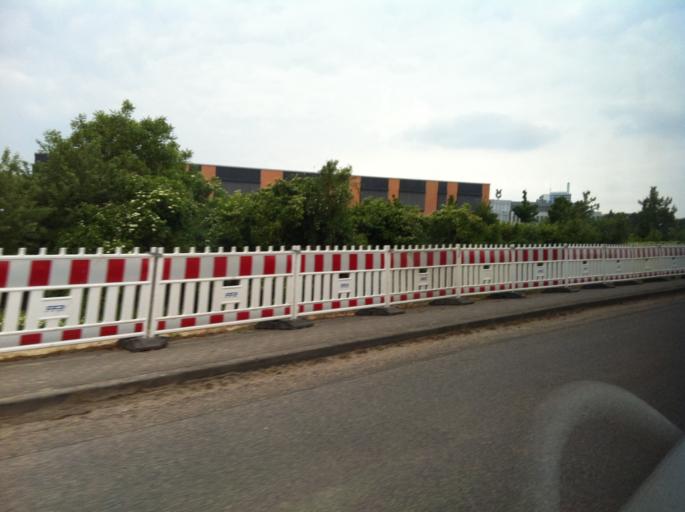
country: DE
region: Rheinland-Pfalz
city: Klein-Winternheim
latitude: 49.9598
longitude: 8.2126
